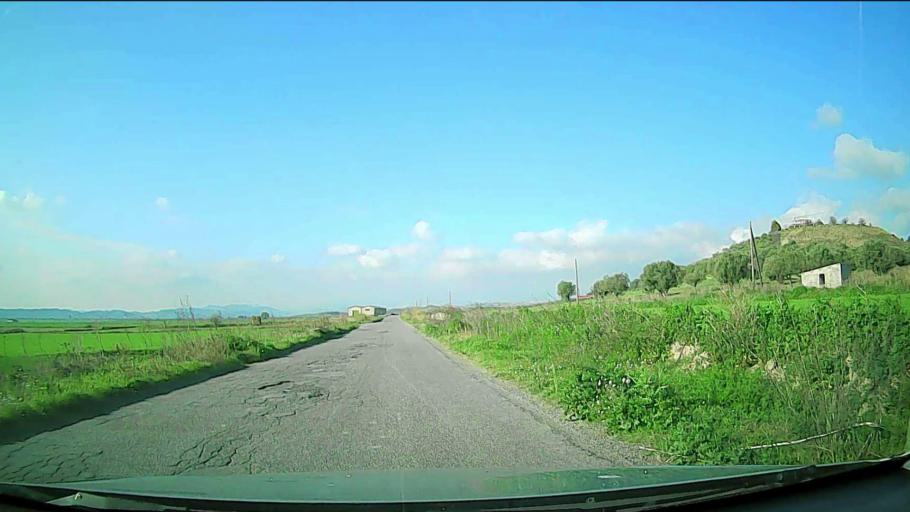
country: IT
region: Calabria
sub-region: Provincia di Crotone
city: Tronca
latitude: 39.2006
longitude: 17.0891
